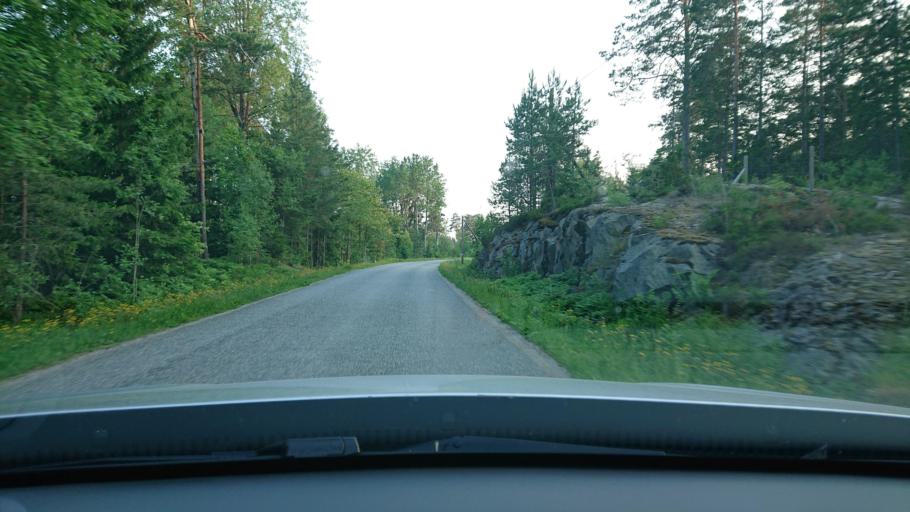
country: SE
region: Stockholm
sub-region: Osterakers Kommun
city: Akersberga
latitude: 59.5176
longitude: 18.3273
